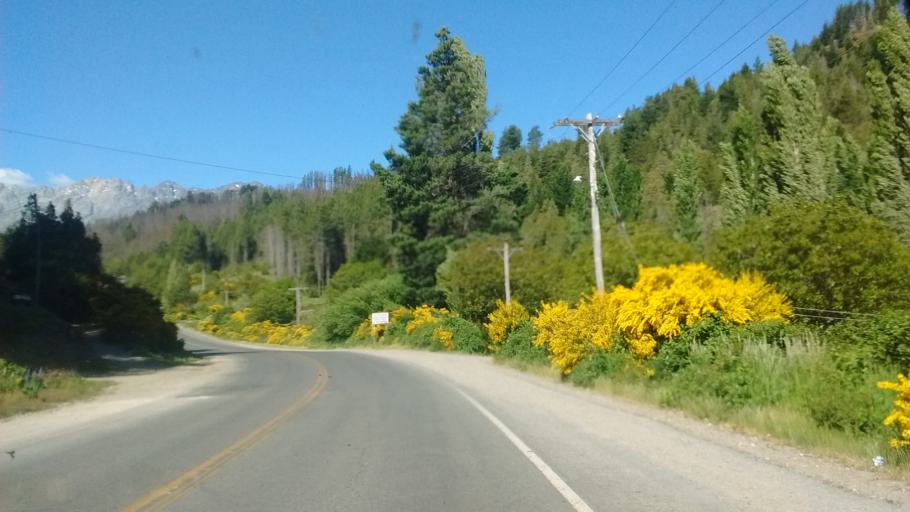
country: AR
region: Chubut
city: Lago Puelo
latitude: -42.0336
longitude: -71.5830
